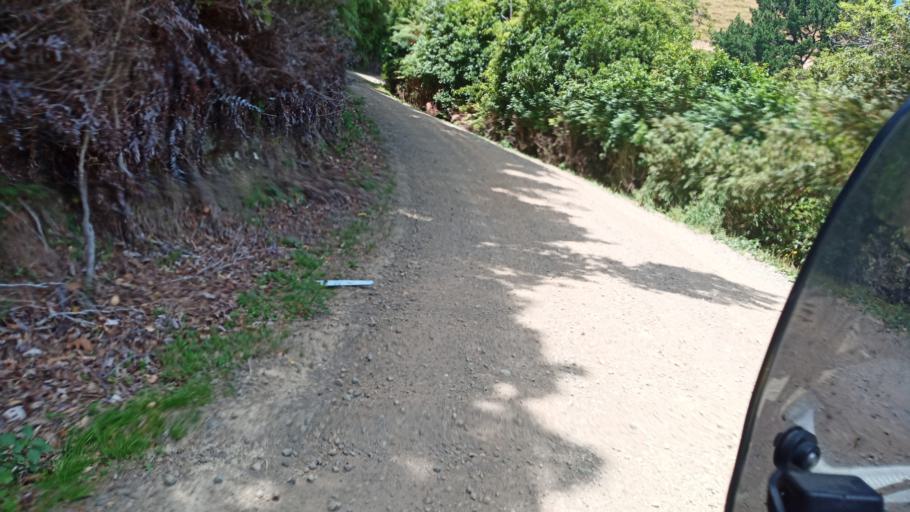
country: NZ
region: Gisborne
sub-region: Gisborne District
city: Gisborne
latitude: -38.4570
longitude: 177.5384
